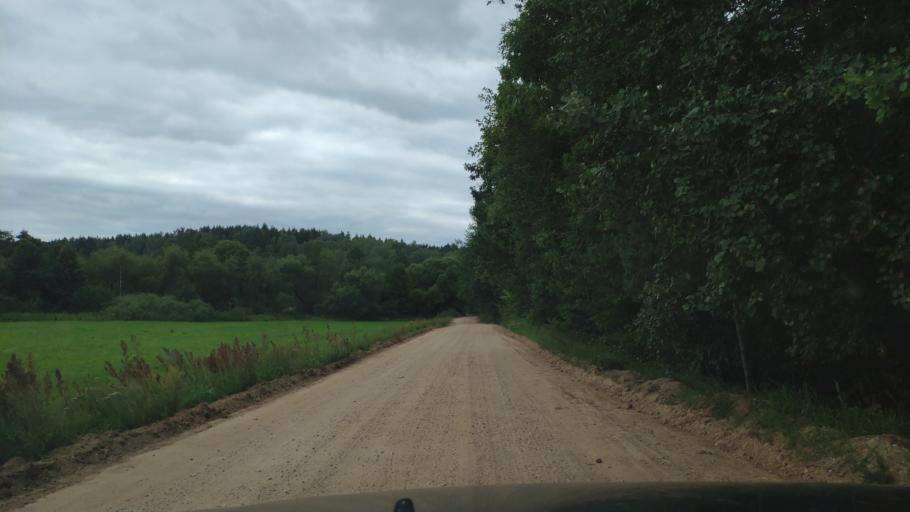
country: BY
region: Minsk
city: Khatsyezhyna
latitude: 53.9353
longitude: 27.2736
